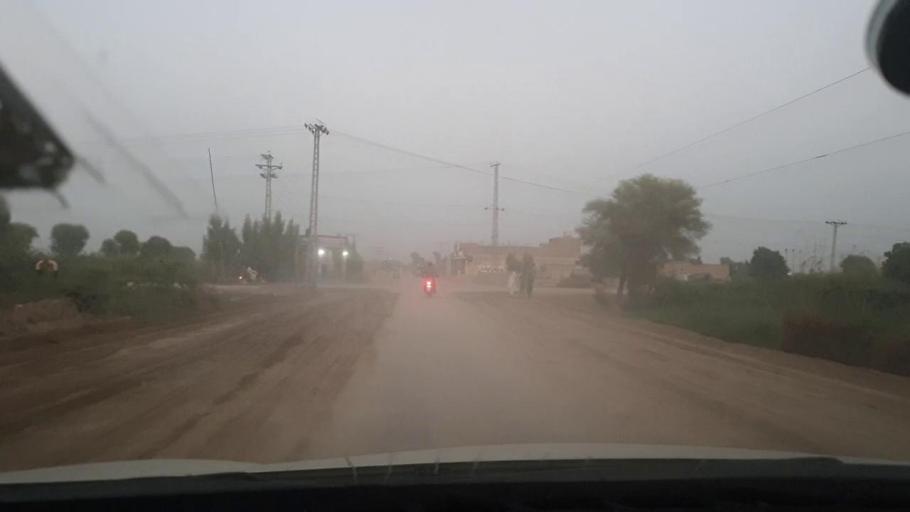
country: PK
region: Sindh
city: Tando Adam
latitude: 25.7595
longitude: 68.6414
